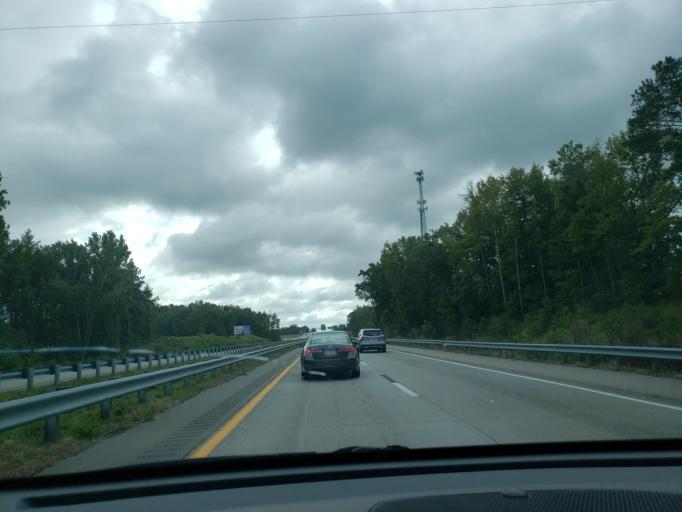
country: US
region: North Carolina
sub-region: Vance County
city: Henderson
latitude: 36.3998
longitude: -78.3331
